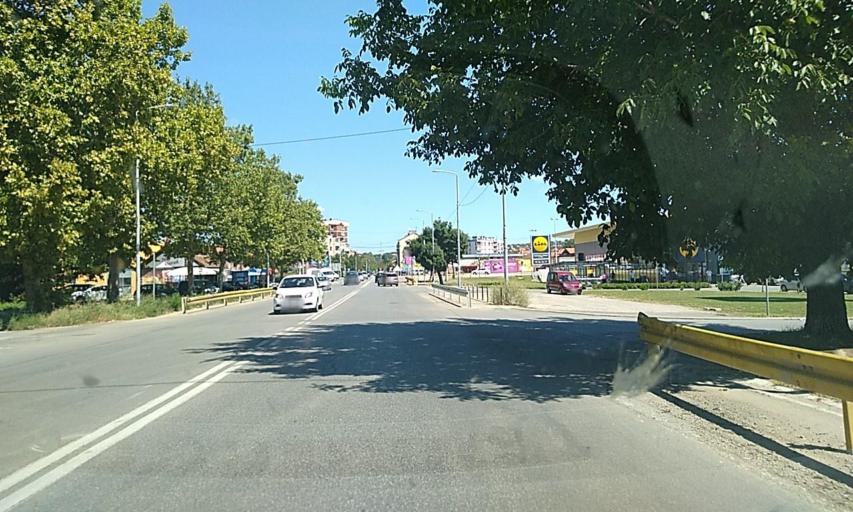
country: RS
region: Central Serbia
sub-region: Branicevski Okrug
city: Pozarevac
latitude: 44.6106
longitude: 21.1736
